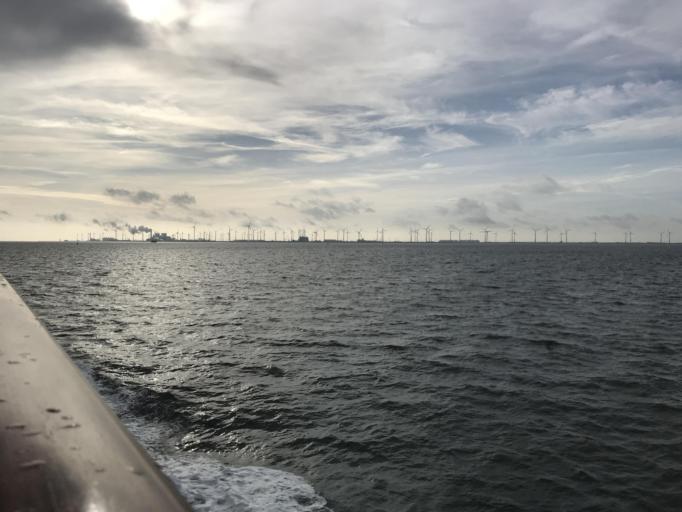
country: DE
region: Lower Saxony
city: Borkum
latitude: 53.5034
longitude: 6.8098
